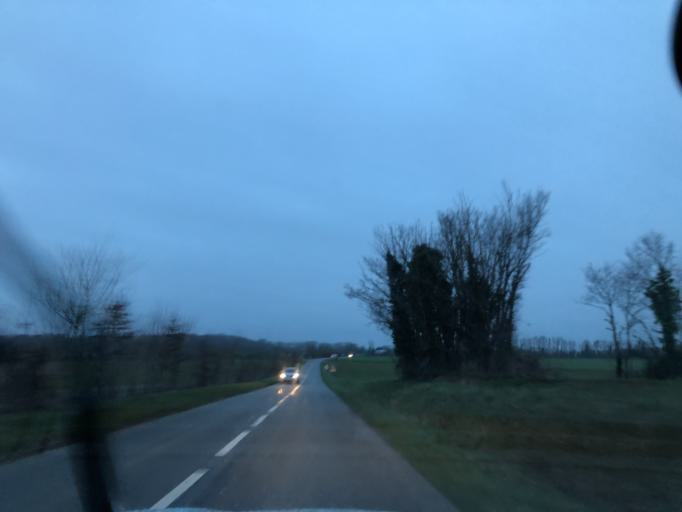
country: FR
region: Lower Normandy
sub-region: Departement du Calvados
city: Blainville-sur-Orne
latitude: 49.2366
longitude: -0.3123
